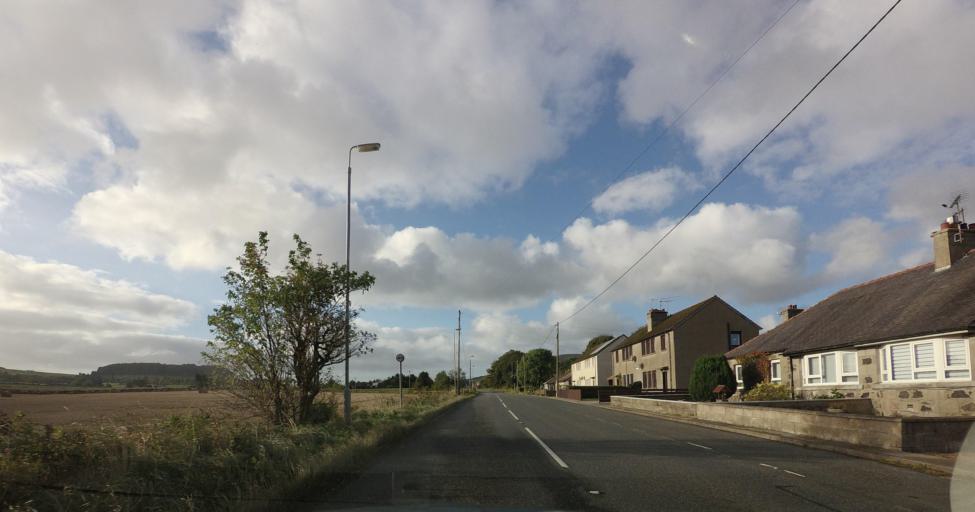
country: GB
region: Scotland
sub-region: Aberdeenshire
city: Portsoy
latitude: 57.5979
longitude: -2.7284
